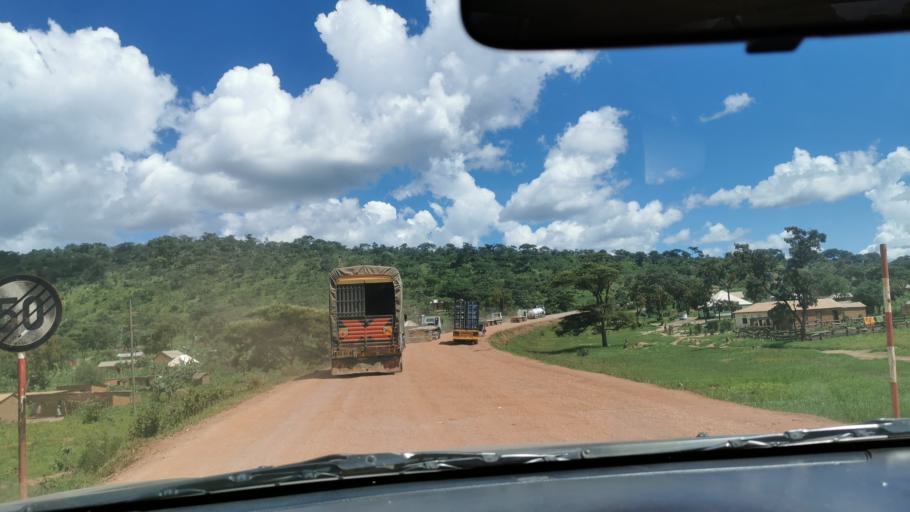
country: TZ
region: Kagera
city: Biharamulo
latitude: -2.8900
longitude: 31.1579
